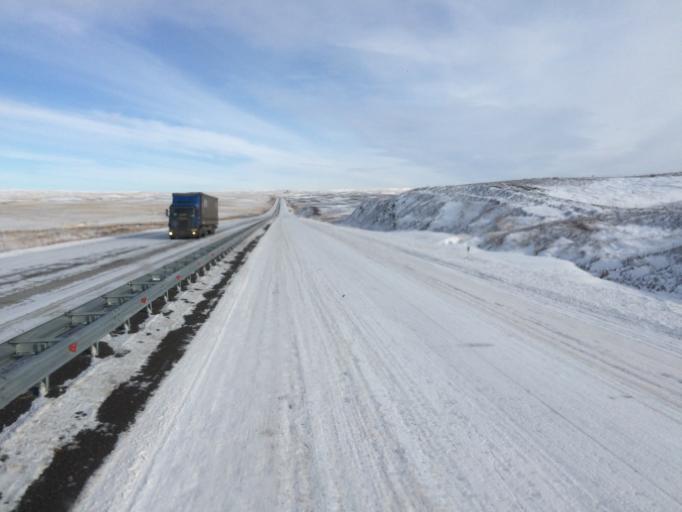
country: KZ
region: Zhambyl
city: Georgiyevka
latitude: 43.3739
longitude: 74.7471
